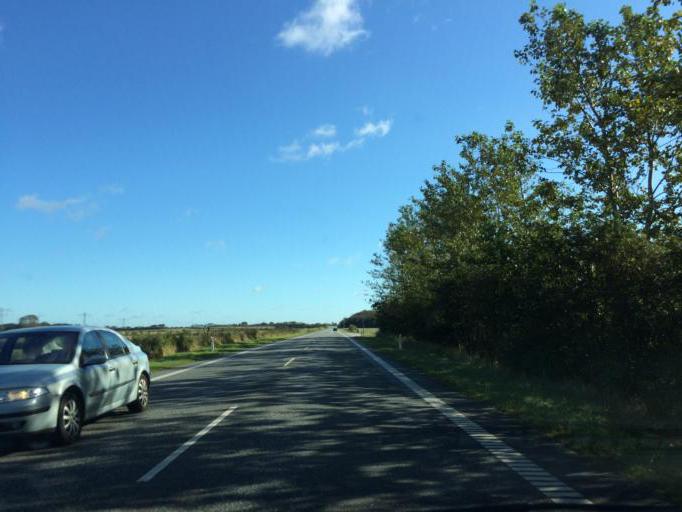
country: DK
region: Central Jutland
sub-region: Holstebro Kommune
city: Vinderup
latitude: 56.3998
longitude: 8.9144
